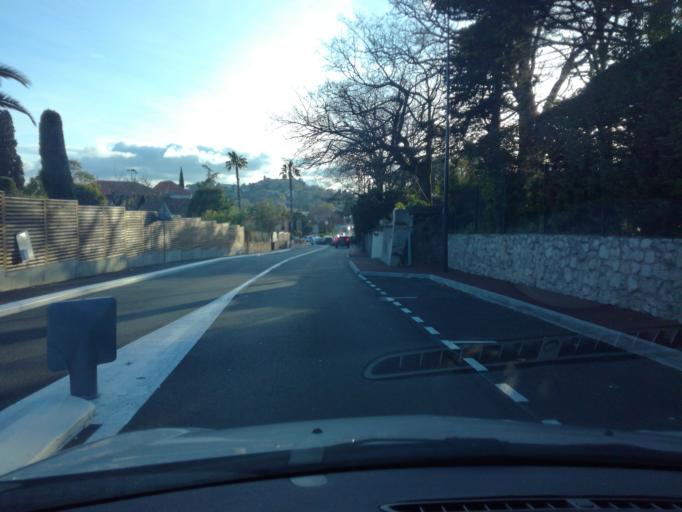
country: FR
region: Provence-Alpes-Cote d'Azur
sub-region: Departement des Alpes-Maritimes
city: Mougins
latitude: 43.6052
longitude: 7.0095
